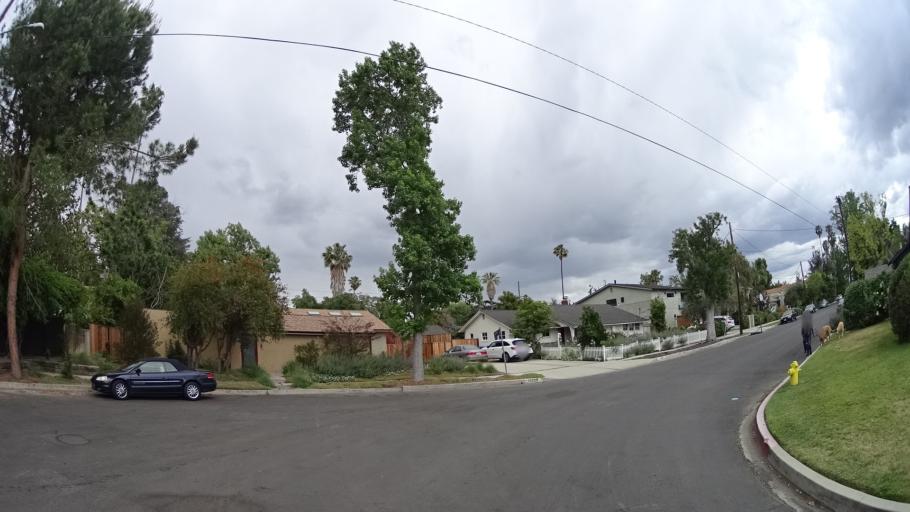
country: US
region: California
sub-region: Los Angeles County
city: Sherman Oaks
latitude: 34.1639
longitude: -118.4213
